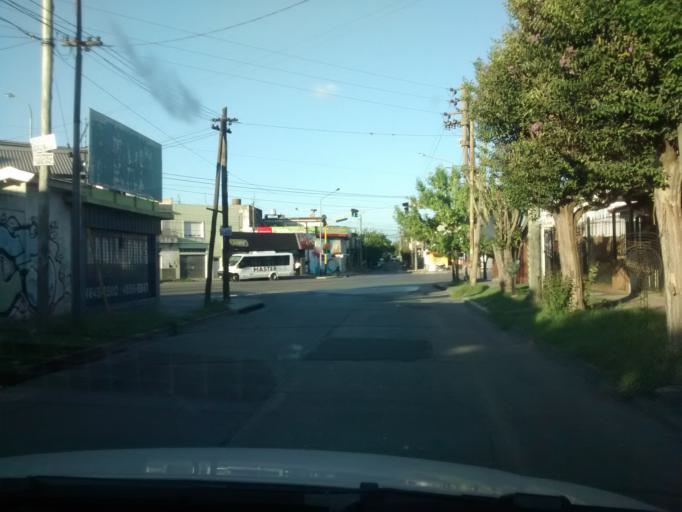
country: AR
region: Buenos Aires
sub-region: Partido de Moron
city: Moron
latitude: -34.6607
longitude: -58.6129
